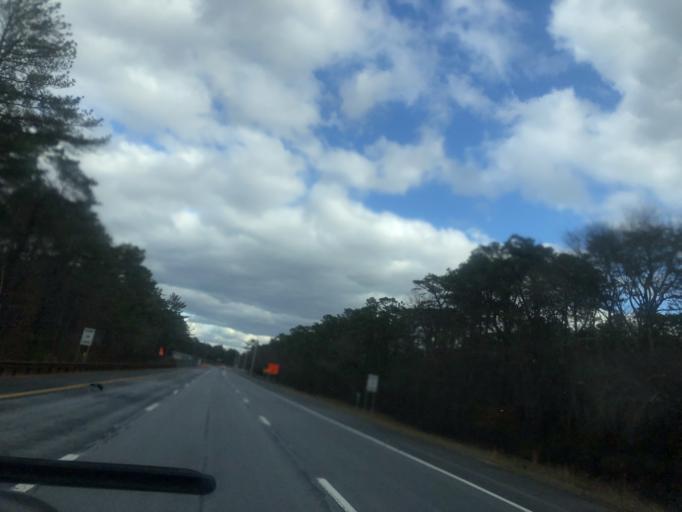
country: US
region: New Jersey
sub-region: Ocean County
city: Mystic Island
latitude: 39.6092
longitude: -74.4293
